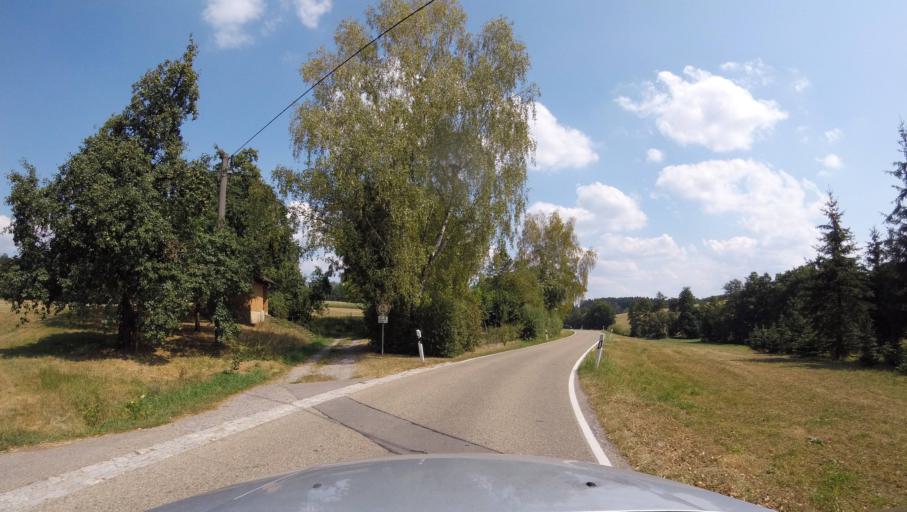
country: DE
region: Baden-Wuerttemberg
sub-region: Regierungsbezirk Stuttgart
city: Althutte
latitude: 48.9476
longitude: 9.5755
